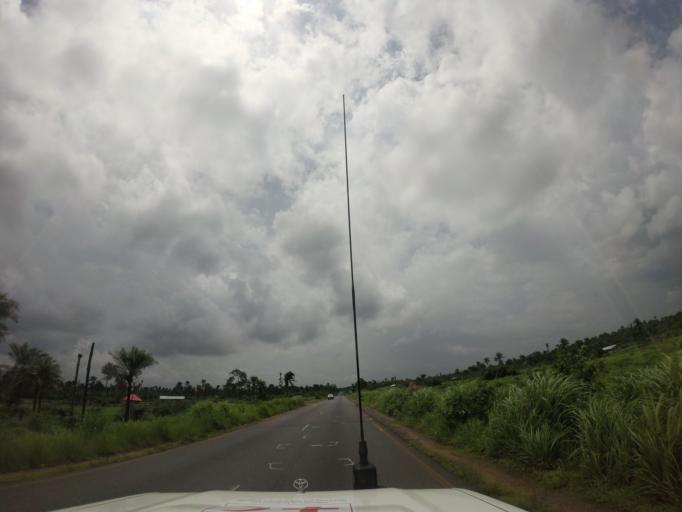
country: SL
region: Northern Province
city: Pepel
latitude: 8.4785
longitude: -12.8198
